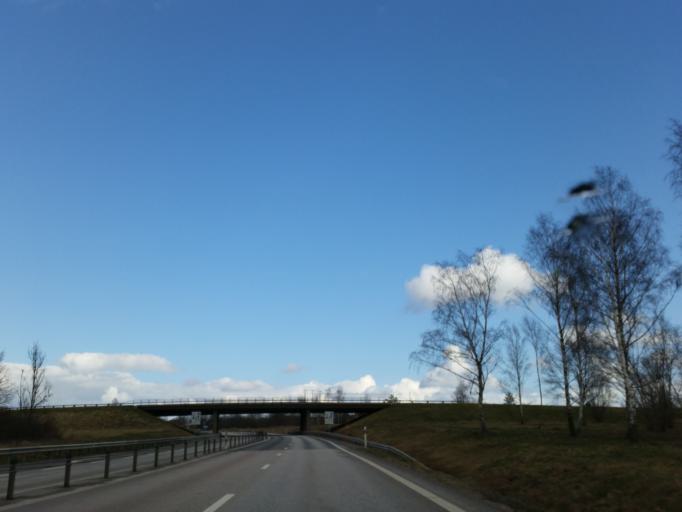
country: SE
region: Kalmar
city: Faerjestaden
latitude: 56.6703
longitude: 16.5121
